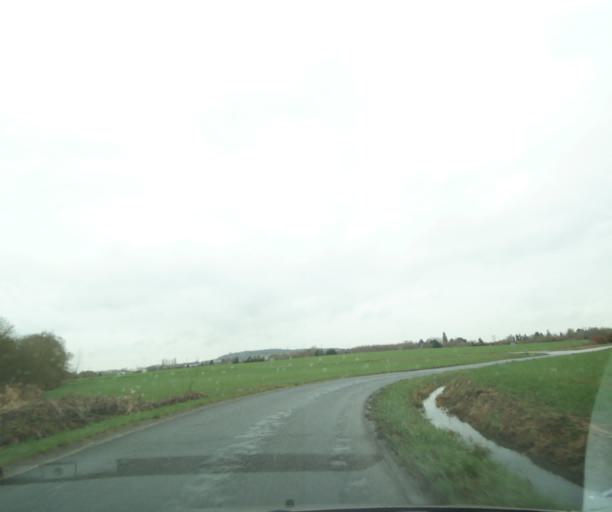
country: FR
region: Picardie
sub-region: Departement de l'Oise
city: Noyon
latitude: 49.5687
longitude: 2.9984
